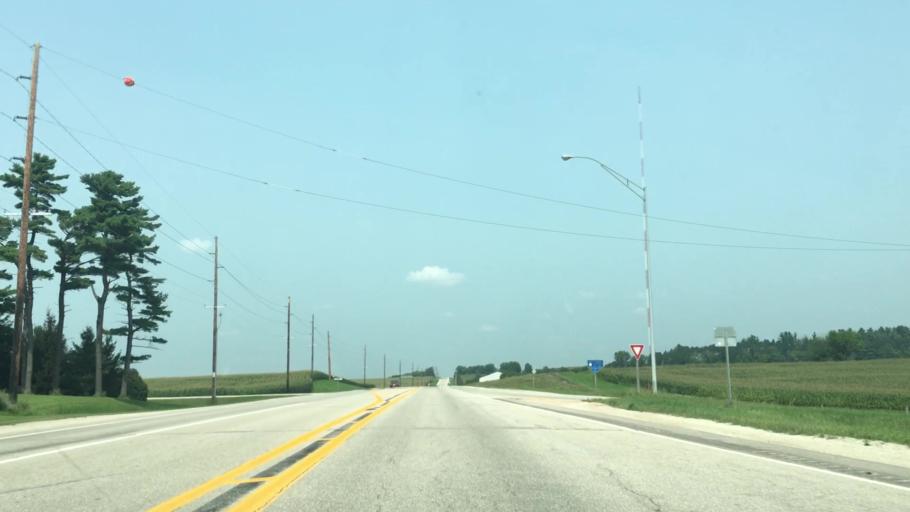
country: US
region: Iowa
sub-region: Benton County
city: Urbana
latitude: 42.2838
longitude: -91.8900
